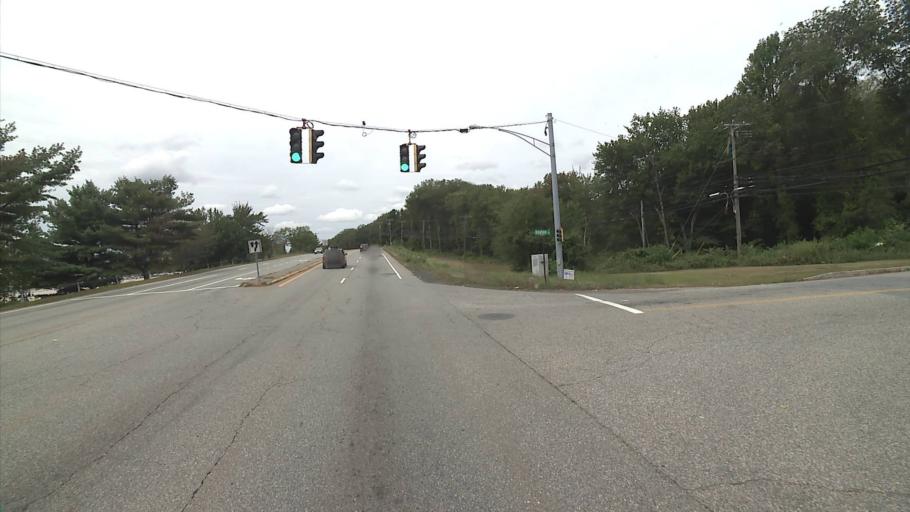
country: US
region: Connecticut
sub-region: New London County
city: Central Waterford
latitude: 41.3748
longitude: -72.1409
